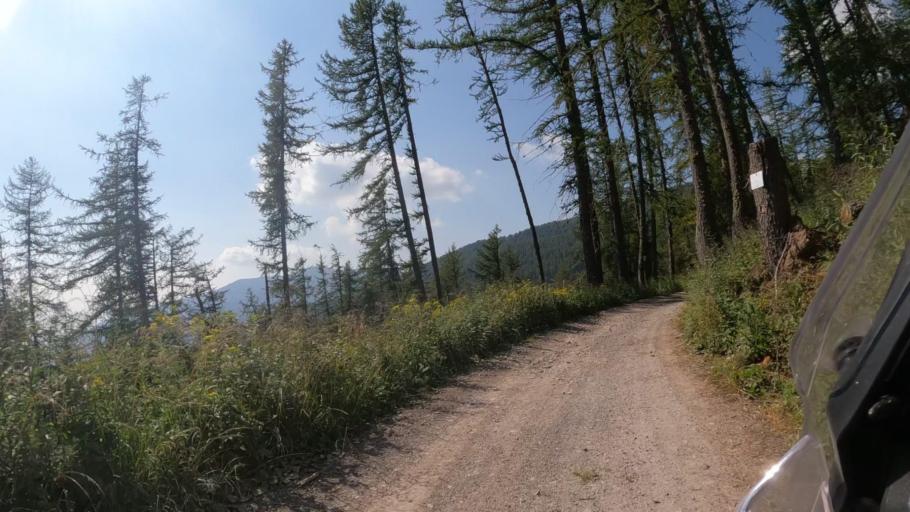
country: IT
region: Piedmont
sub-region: Provincia di Cuneo
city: Briga Alta
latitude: 44.0957
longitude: 7.7228
